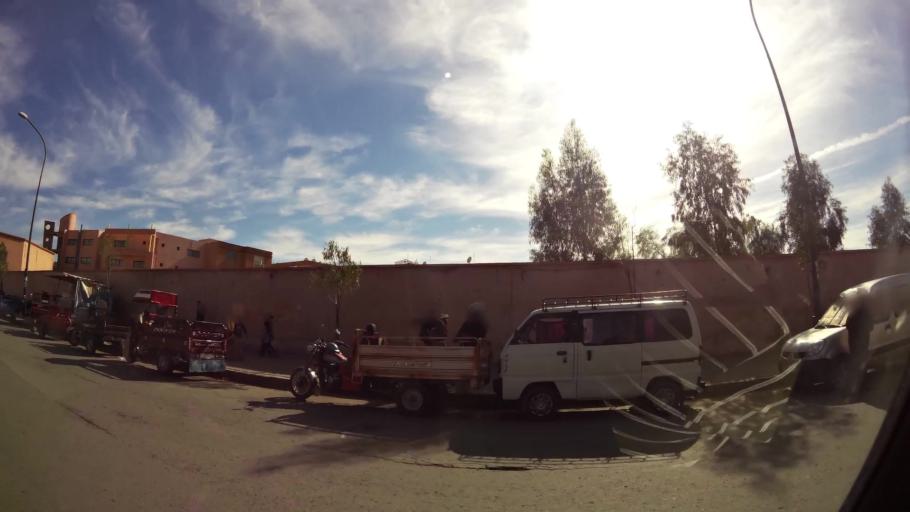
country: MA
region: Marrakech-Tensift-Al Haouz
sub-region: Marrakech
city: Marrakesh
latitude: 31.6063
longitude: -7.9633
